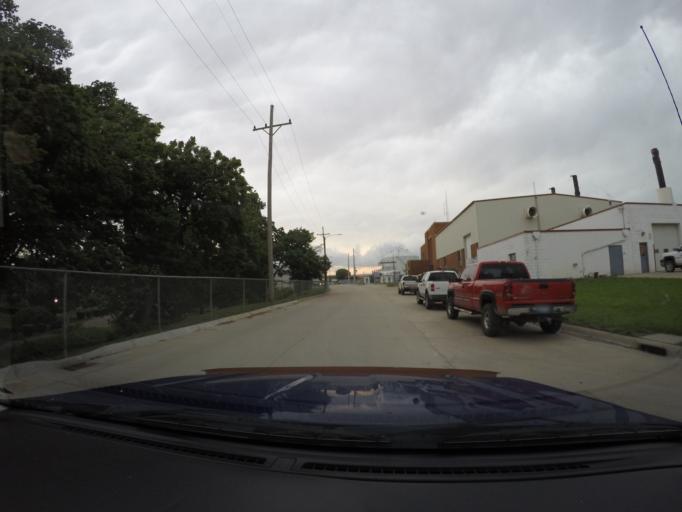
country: US
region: Kansas
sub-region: Clay County
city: Clay Center
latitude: 39.3732
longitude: -97.1281
